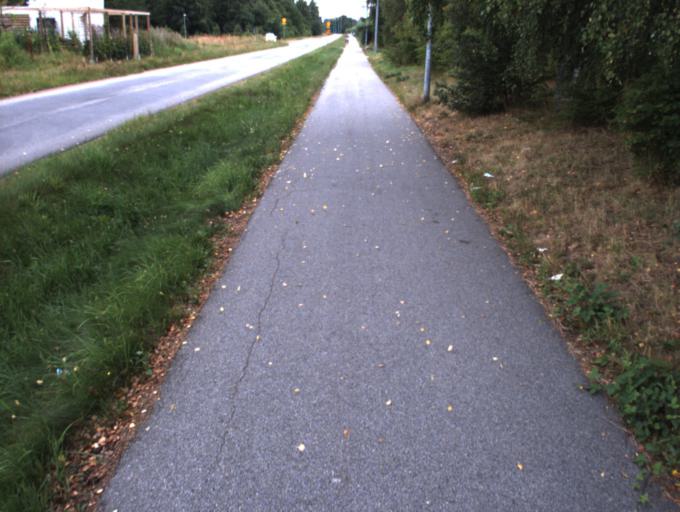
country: SE
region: Skane
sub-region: Helsingborg
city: Odakra
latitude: 56.0593
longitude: 12.7358
